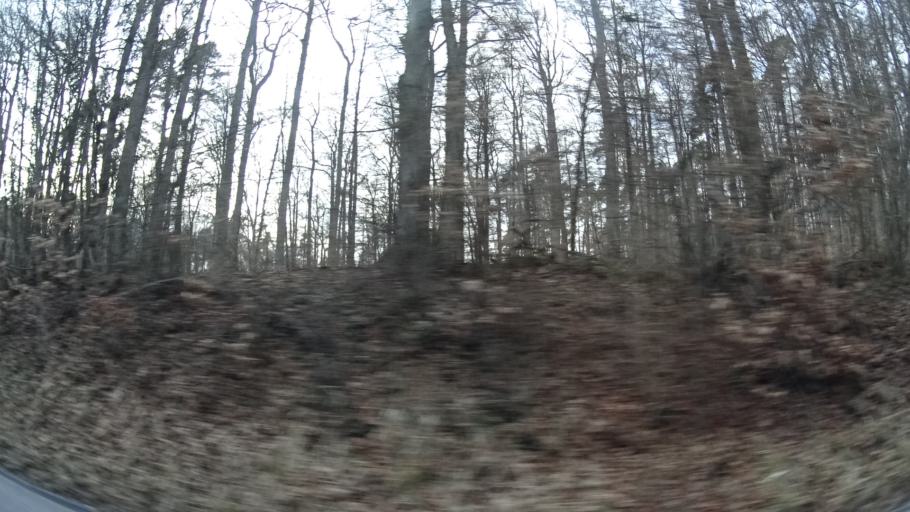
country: DE
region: Baden-Wuerttemberg
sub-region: Regierungsbezirk Stuttgart
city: Gerlingen
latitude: 48.7769
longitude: 9.0615
